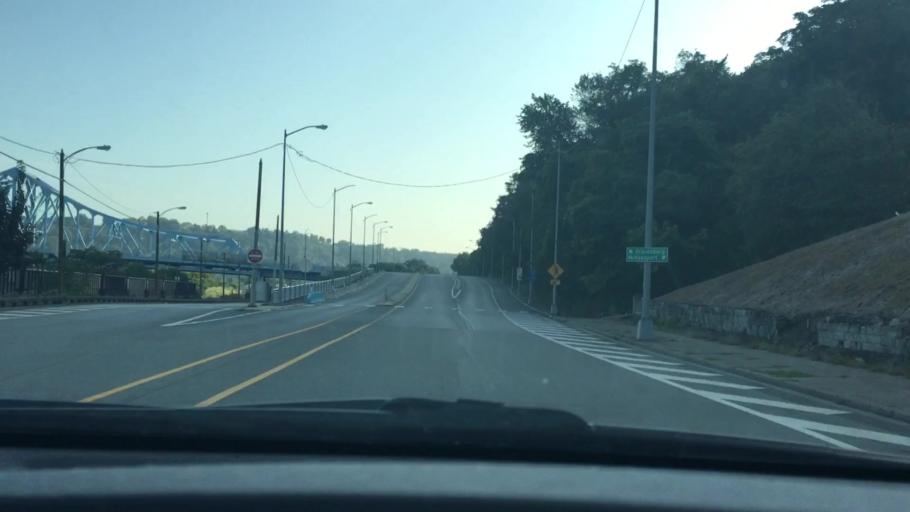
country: US
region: Pennsylvania
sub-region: Allegheny County
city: Dravosburg
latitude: 40.3425
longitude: -79.8857
